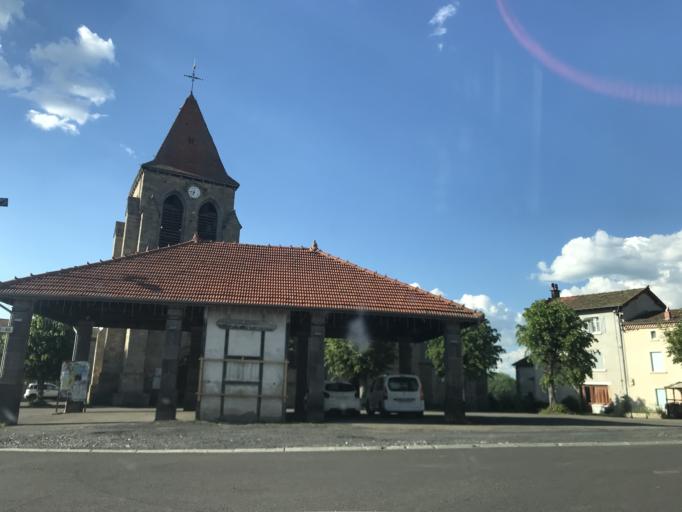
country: FR
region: Auvergne
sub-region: Departement du Puy-de-Dome
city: Job
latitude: 45.6178
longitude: 3.6807
